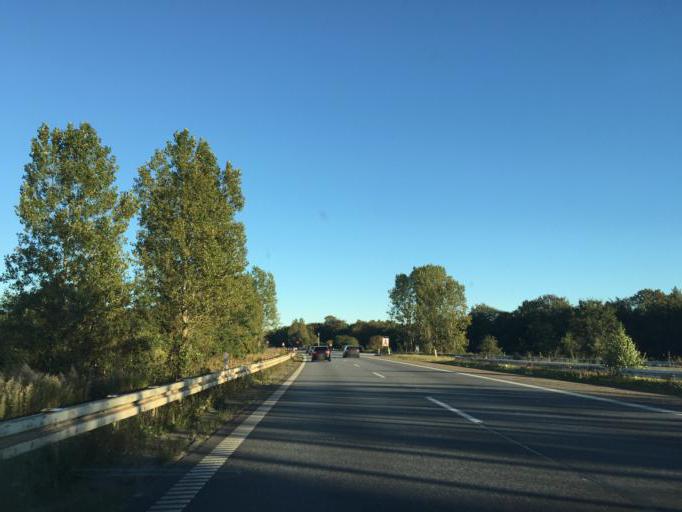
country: DK
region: Capital Region
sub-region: Fureso Kommune
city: Vaerlose
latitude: 55.7774
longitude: 12.4021
